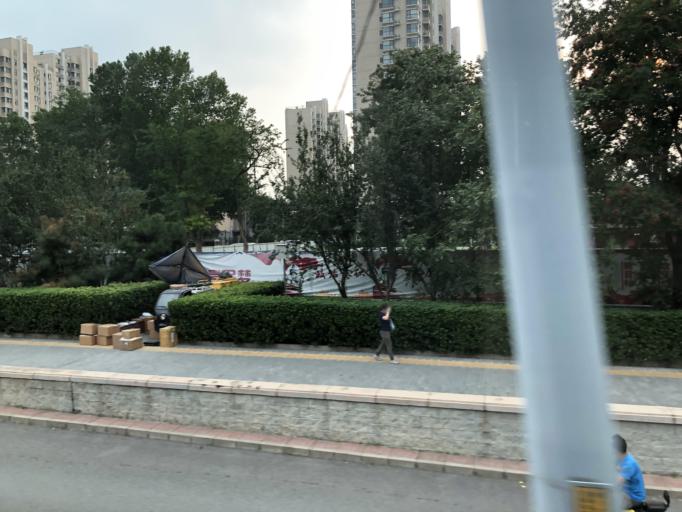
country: CN
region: Beijing
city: Jinrongjie
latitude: 39.9365
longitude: 116.3193
